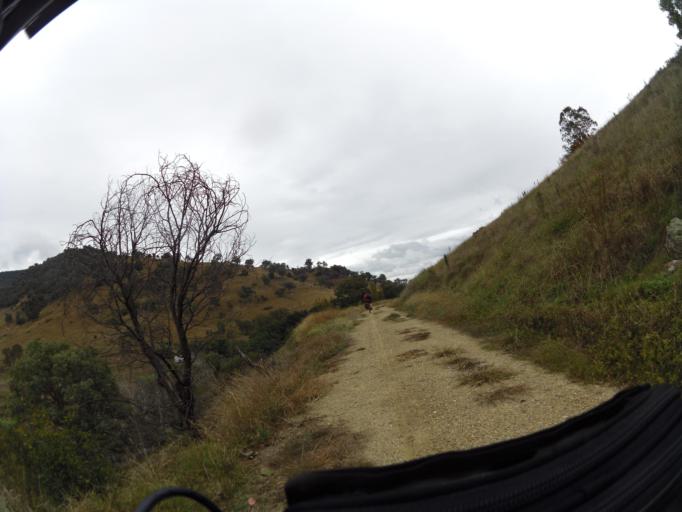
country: AU
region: New South Wales
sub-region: Albury Municipality
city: East Albury
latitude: -36.1855
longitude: 147.3576
